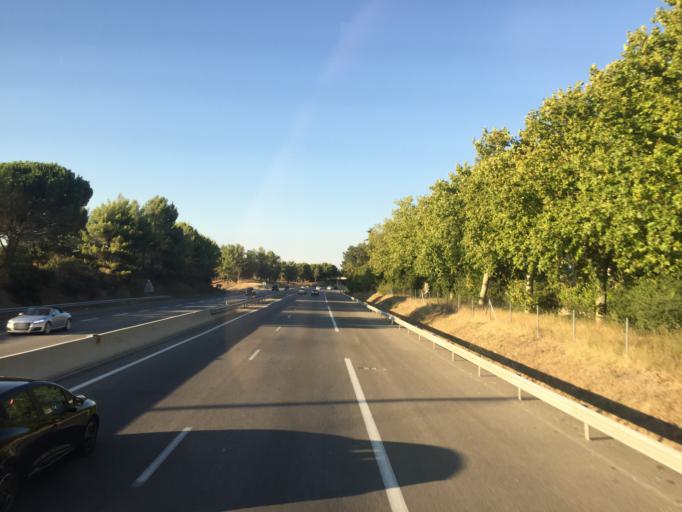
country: FR
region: Provence-Alpes-Cote d'Azur
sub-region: Departement des Bouches-du-Rhone
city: Venelles
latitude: 43.5697
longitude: 5.4666
